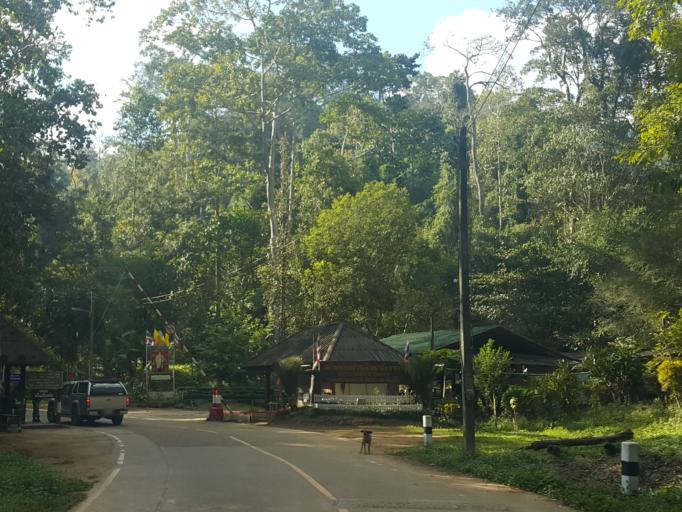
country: TH
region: Chiang Mai
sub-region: Amphoe Chiang Dao
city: Chiang Dao
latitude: 19.4139
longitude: 98.9155
